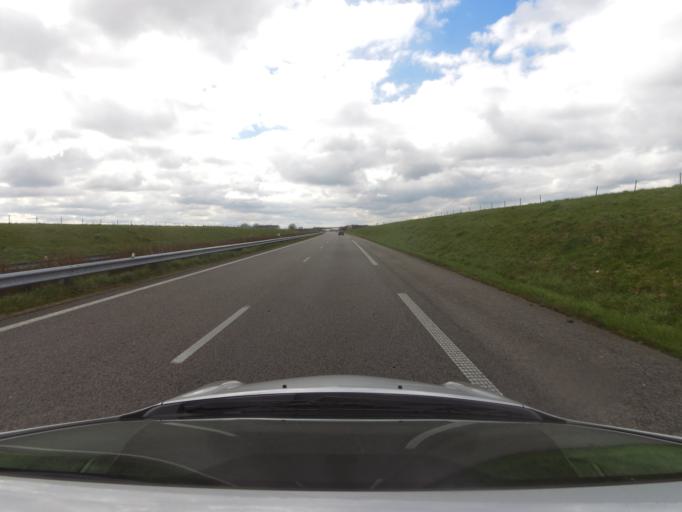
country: FR
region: Haute-Normandie
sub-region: Departement de la Seine-Maritime
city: Lanquetot
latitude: 49.6095
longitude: 0.5106
